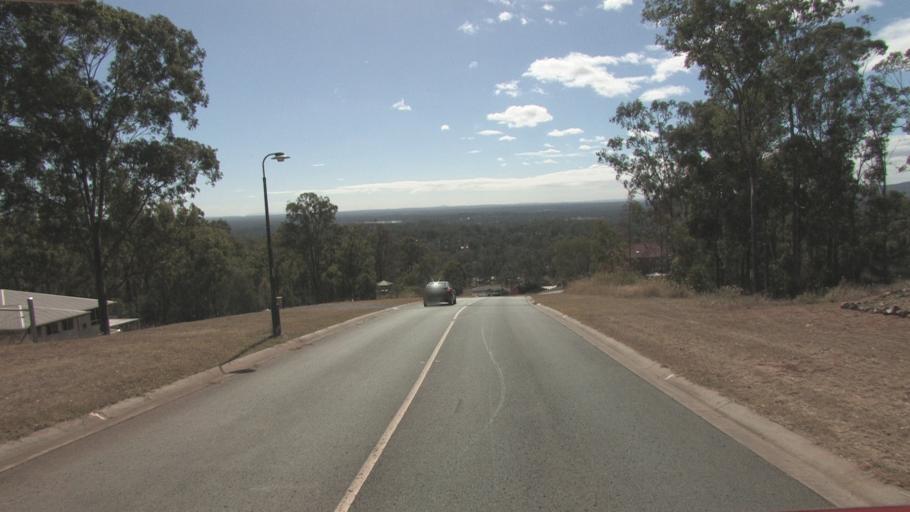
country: AU
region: Queensland
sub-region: Logan
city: Cedar Vale
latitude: -27.8914
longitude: 153.0026
